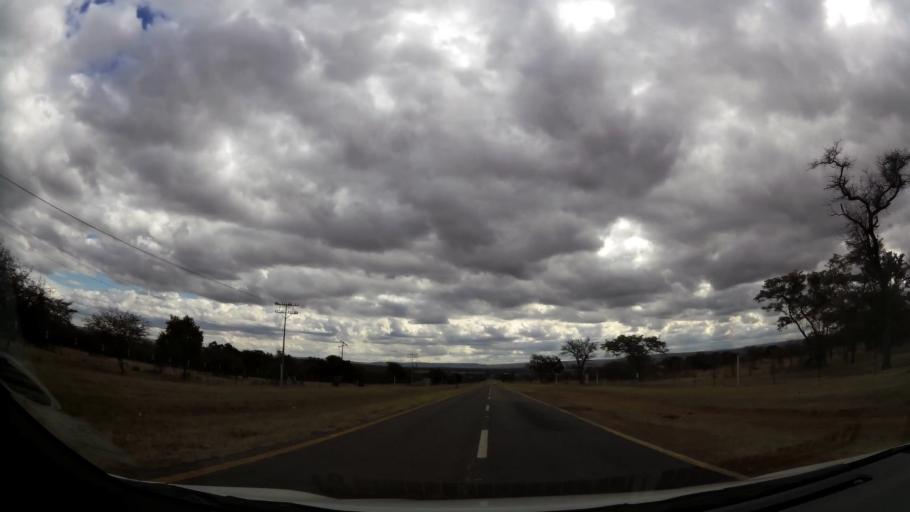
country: ZA
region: Limpopo
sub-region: Waterberg District Municipality
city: Modimolle
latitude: -24.7608
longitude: 28.4567
